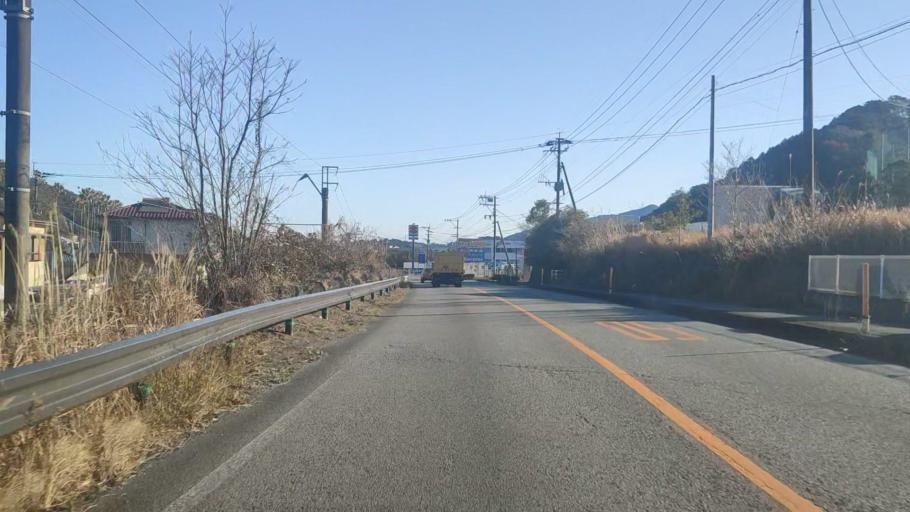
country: JP
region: Miyazaki
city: Nobeoka
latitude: 32.5031
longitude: 131.6675
